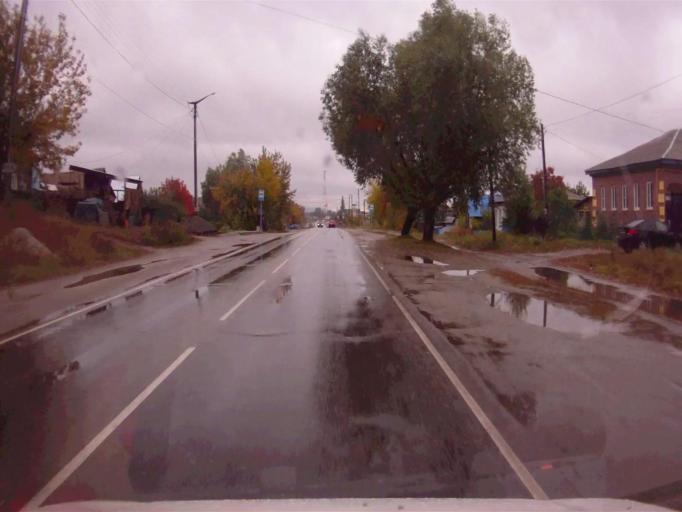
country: RU
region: Chelyabinsk
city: Kyshtym
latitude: 55.7128
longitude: 60.5581
